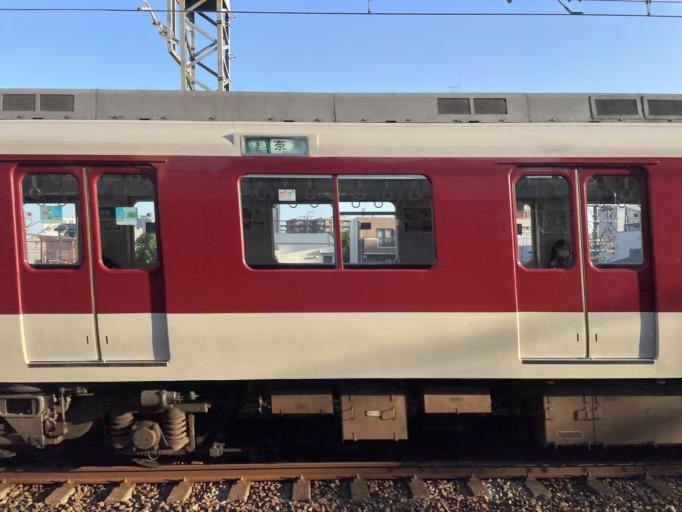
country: JP
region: Osaka
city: Osaka-shi
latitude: 34.6656
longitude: 135.5385
